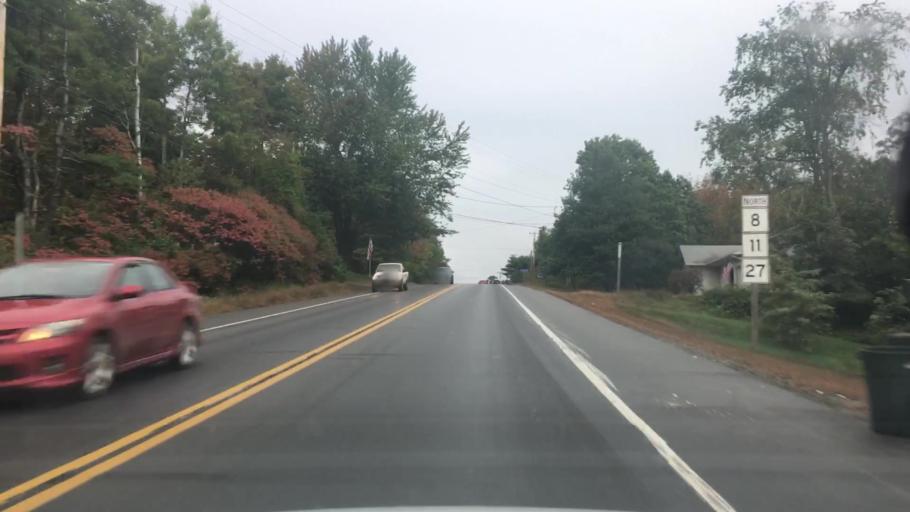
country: US
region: Maine
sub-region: Kennebec County
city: Belgrade
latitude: 44.3888
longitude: -69.8026
